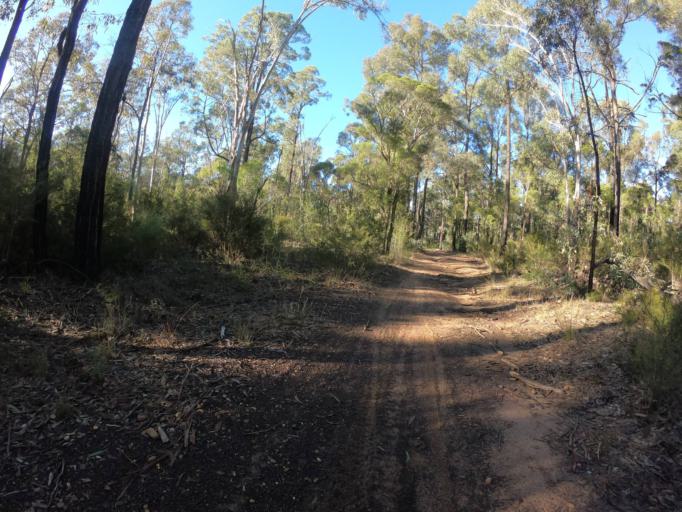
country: AU
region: New South Wales
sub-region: Hawkesbury
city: South Windsor
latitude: -33.6475
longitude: 150.8041
